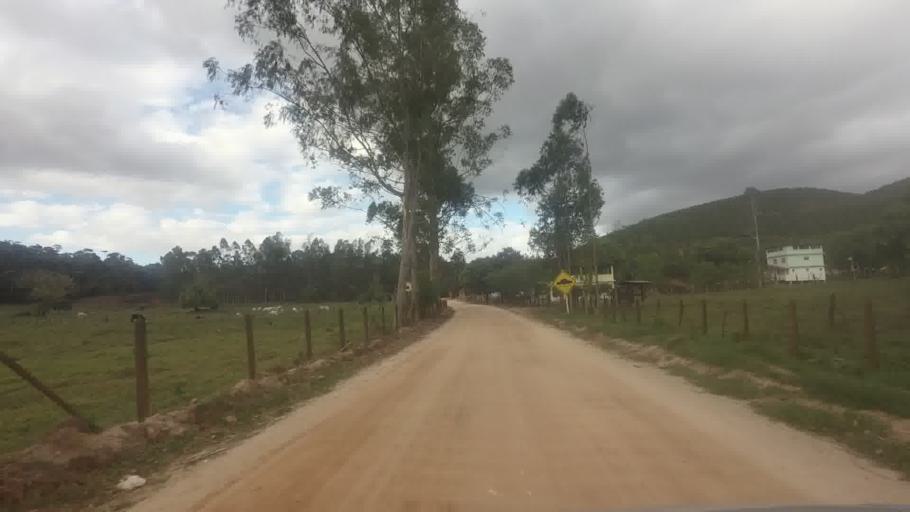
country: BR
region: Espirito Santo
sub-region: Mimoso Do Sul
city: Mimoso do Sul
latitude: -20.9517
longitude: -41.4230
